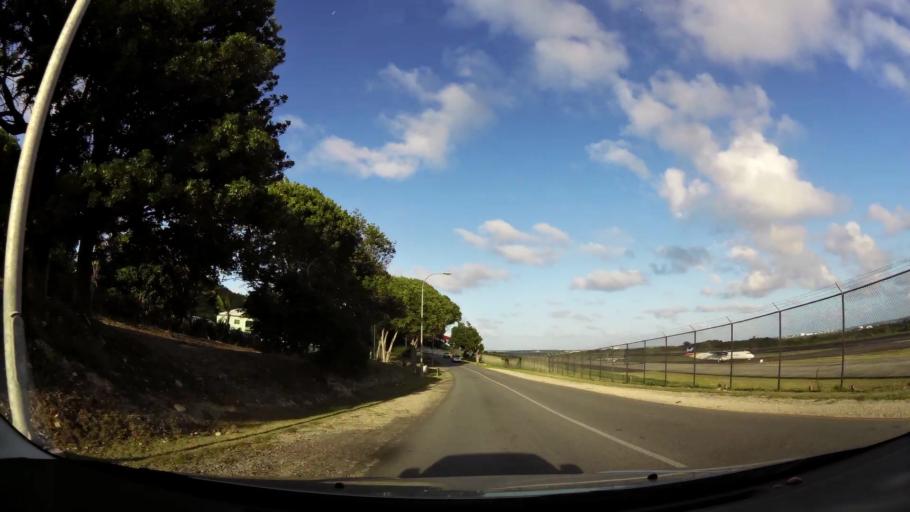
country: AG
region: Saint George
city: Piggotts
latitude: 17.1346
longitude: -61.7996
